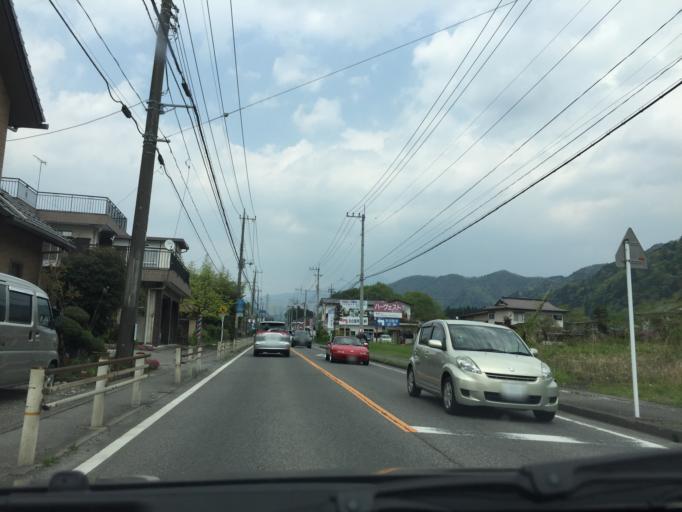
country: JP
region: Tochigi
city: Imaichi
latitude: 36.8009
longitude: 139.7064
